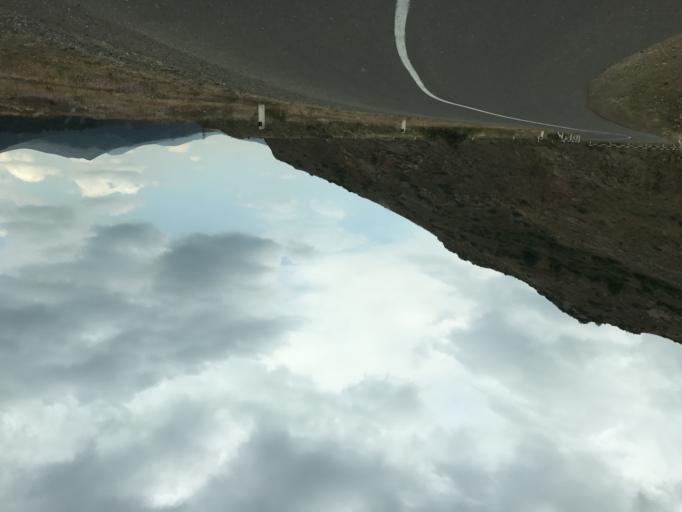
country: AZ
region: Susa
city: Shushi
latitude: 39.7181
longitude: 46.6707
